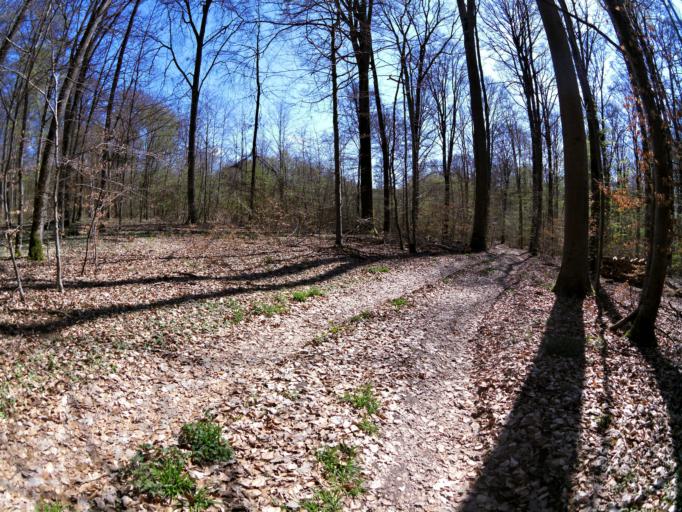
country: DE
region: Bavaria
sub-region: Regierungsbezirk Unterfranken
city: Hettstadt
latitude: 49.8212
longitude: 9.8104
